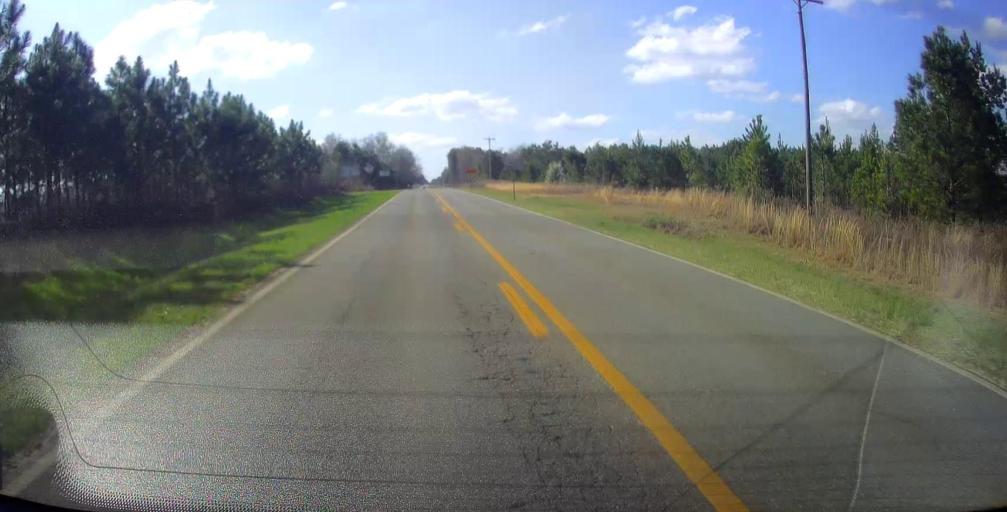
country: US
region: Georgia
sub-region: Laurens County
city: Dublin
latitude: 32.5615
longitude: -83.0127
